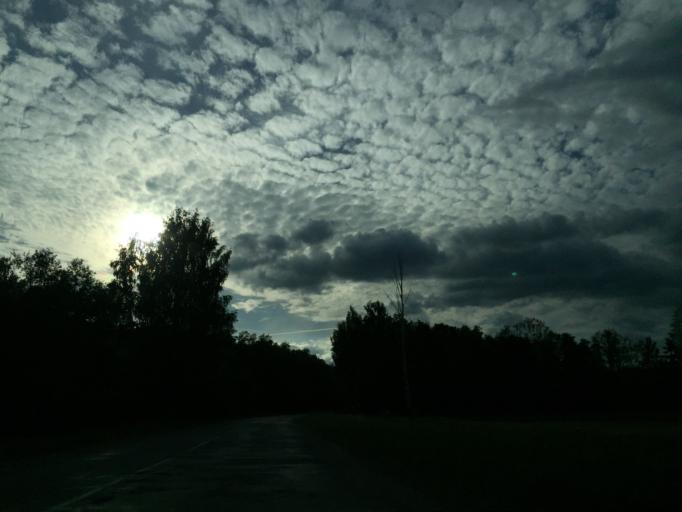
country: LV
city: Tireli
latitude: 56.8359
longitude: 23.5473
